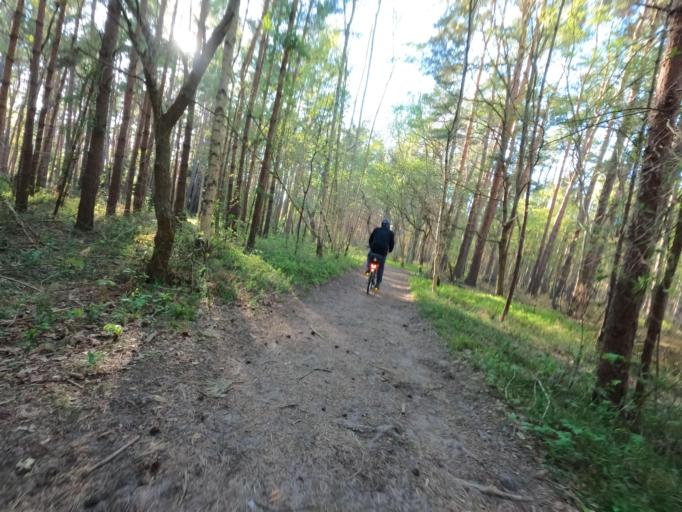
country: DE
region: Mecklenburg-Vorpommern
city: Born
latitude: 54.3949
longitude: 12.5328
